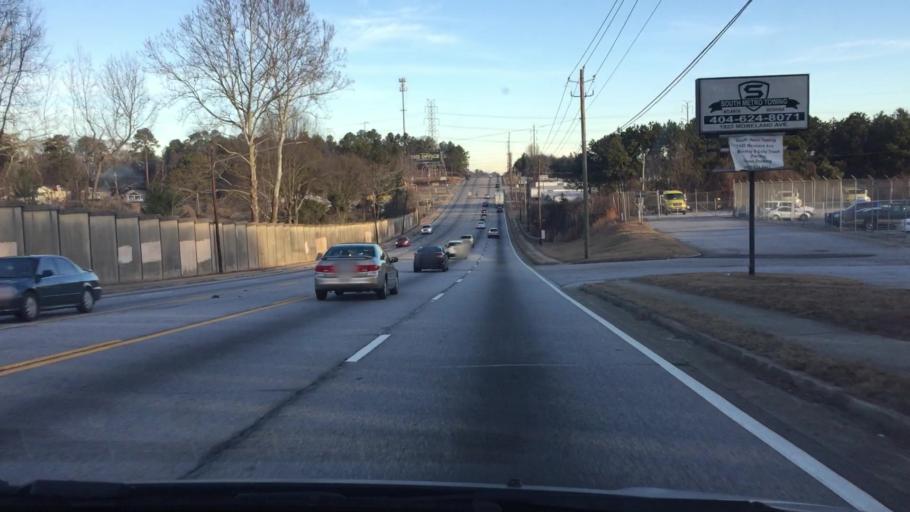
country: US
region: Georgia
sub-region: DeKalb County
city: Gresham Park
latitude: 33.7059
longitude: -84.3494
